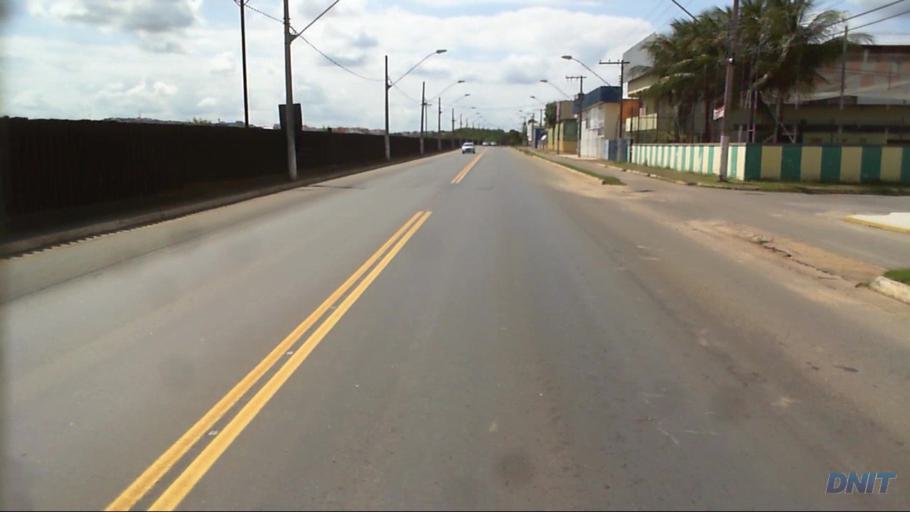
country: BR
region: Minas Gerais
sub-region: Governador Valadares
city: Governador Valadares
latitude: -18.8946
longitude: -41.9797
